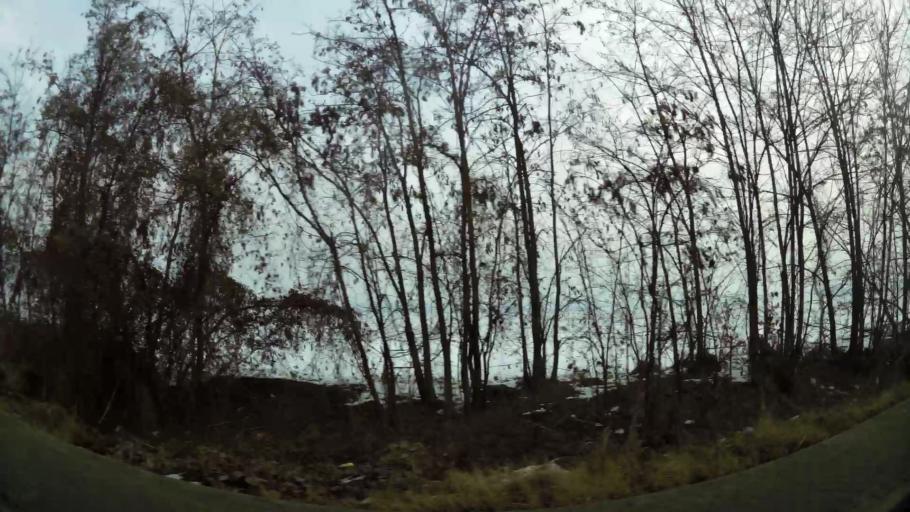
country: MK
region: Kisela Voda
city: Kisela Voda
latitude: 41.9875
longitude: 21.5162
